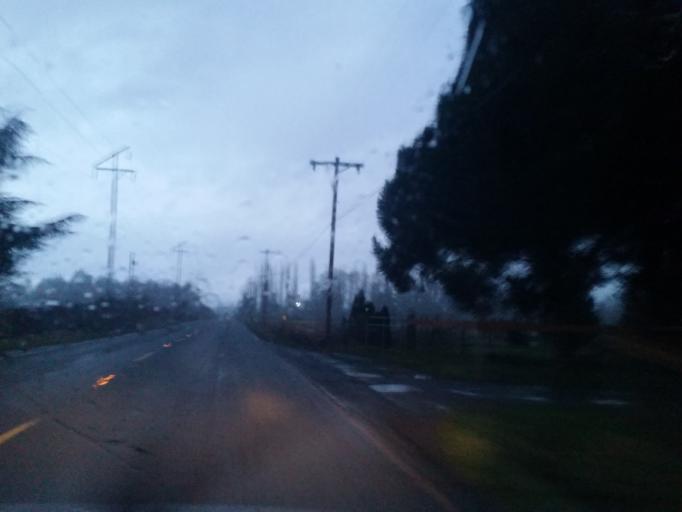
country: US
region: Washington
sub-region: Snohomish County
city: Everett
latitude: 47.9639
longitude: -122.1738
